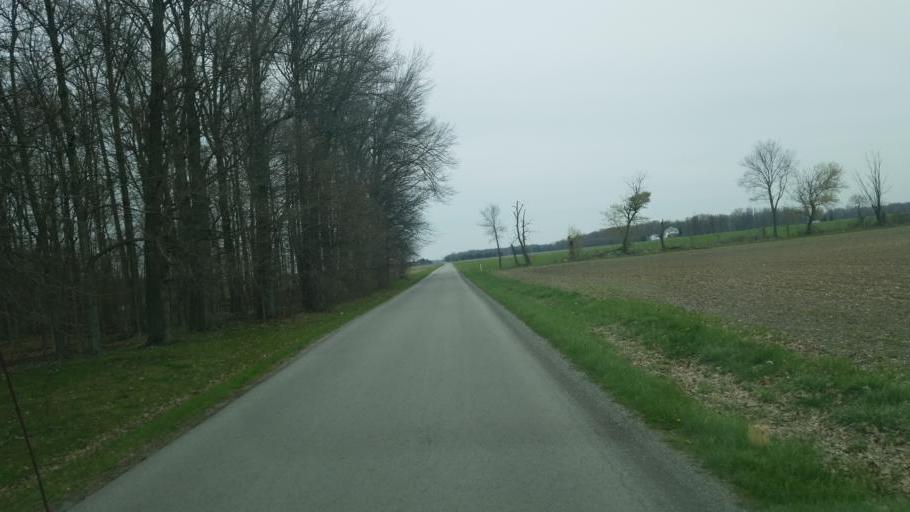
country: US
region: Ohio
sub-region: Wyandot County
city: Carey
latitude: 40.9694
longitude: -83.5129
